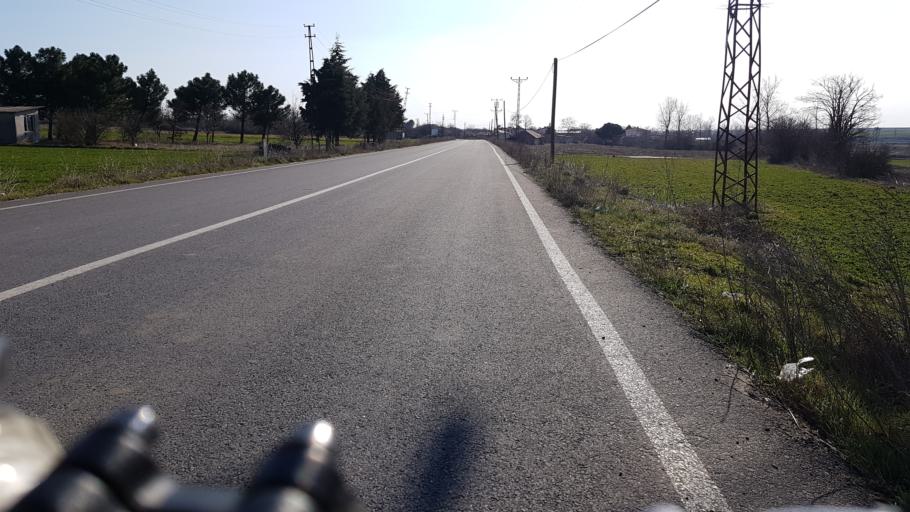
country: TR
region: Tekirdag
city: Velimese
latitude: 41.3489
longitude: 27.8381
